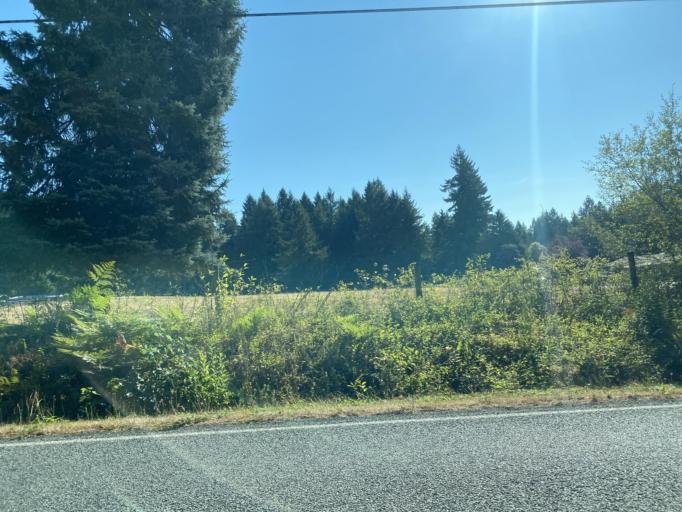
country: US
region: Washington
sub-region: Thurston County
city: Tanglewilde-Thompson Place
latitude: 47.0004
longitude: -122.7386
